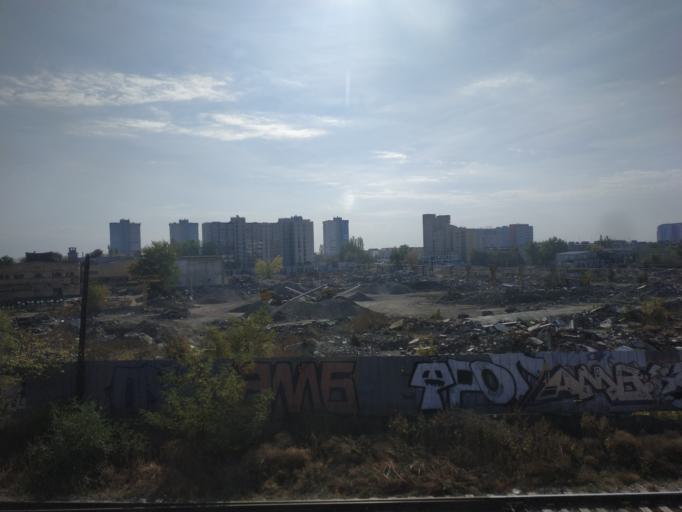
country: RU
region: Volgograd
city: Volgograd
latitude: 48.7333
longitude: 44.5364
